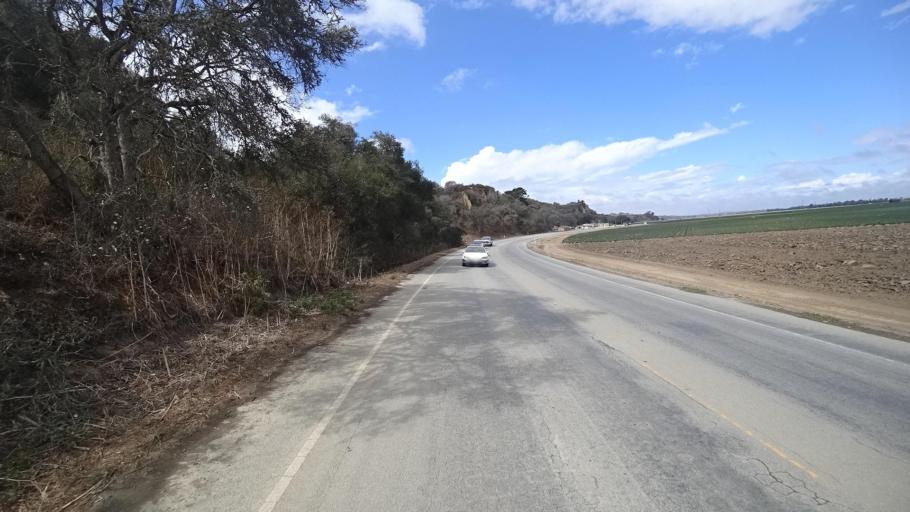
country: US
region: California
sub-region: Monterey County
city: Salinas
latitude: 36.6428
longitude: -121.7130
